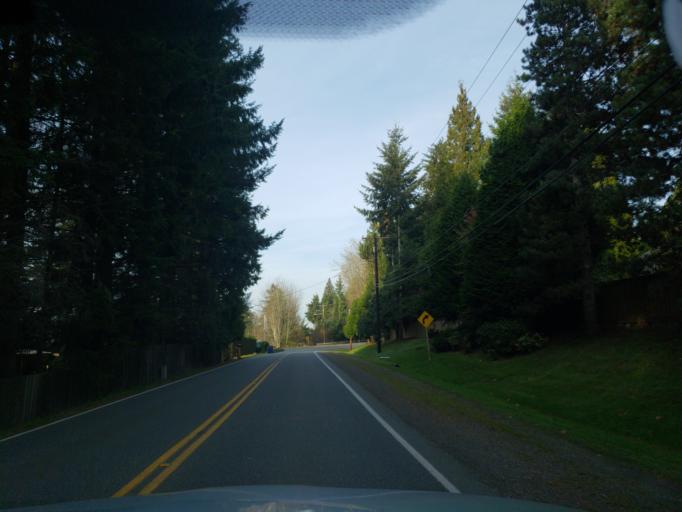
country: US
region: Washington
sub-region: Snohomish County
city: Maltby
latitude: 47.7920
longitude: -122.1330
